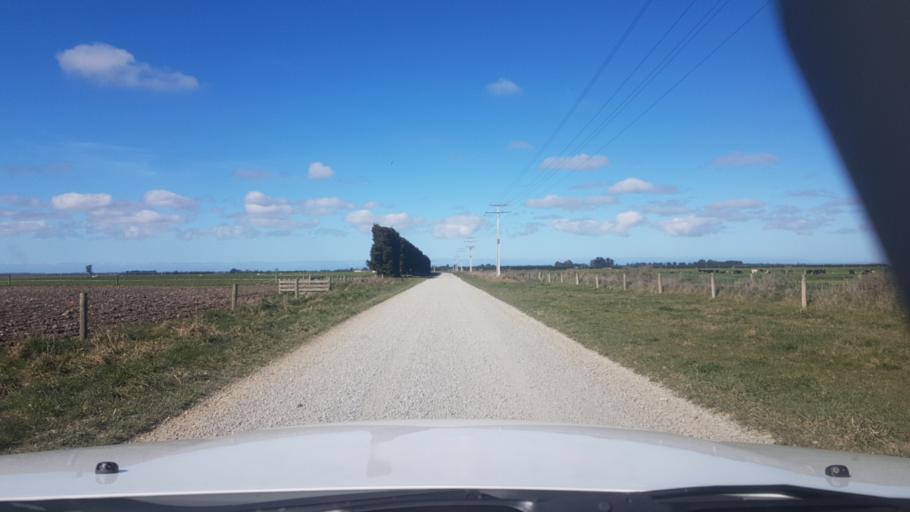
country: NZ
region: Canterbury
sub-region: Timaru District
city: Pleasant Point
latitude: -44.0806
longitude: 171.3699
